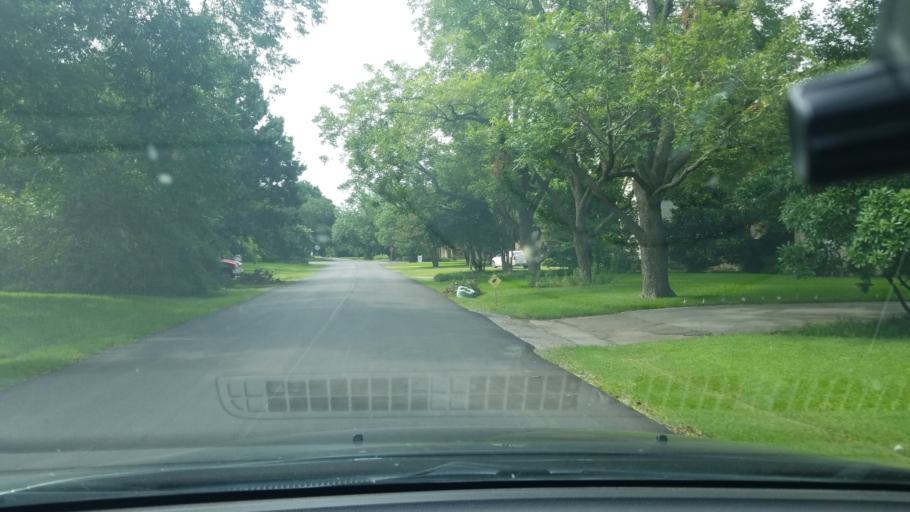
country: US
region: Texas
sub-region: Dallas County
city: Highland Park
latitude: 32.8262
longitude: -96.7017
